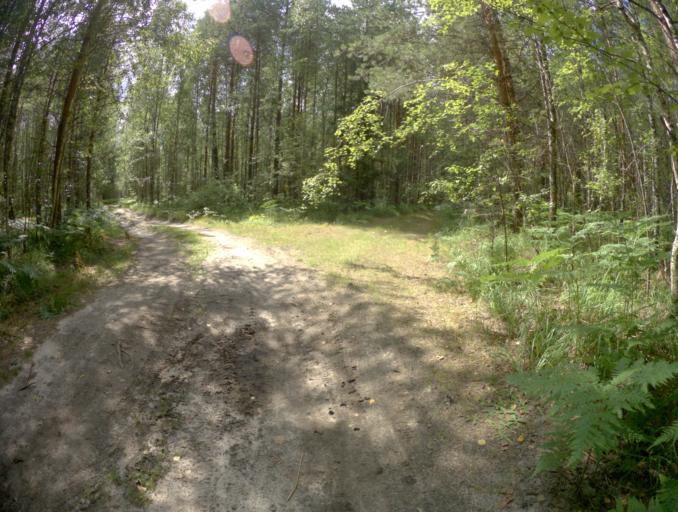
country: RU
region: Vladimir
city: Raduzhnyy
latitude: 55.9525
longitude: 40.1976
